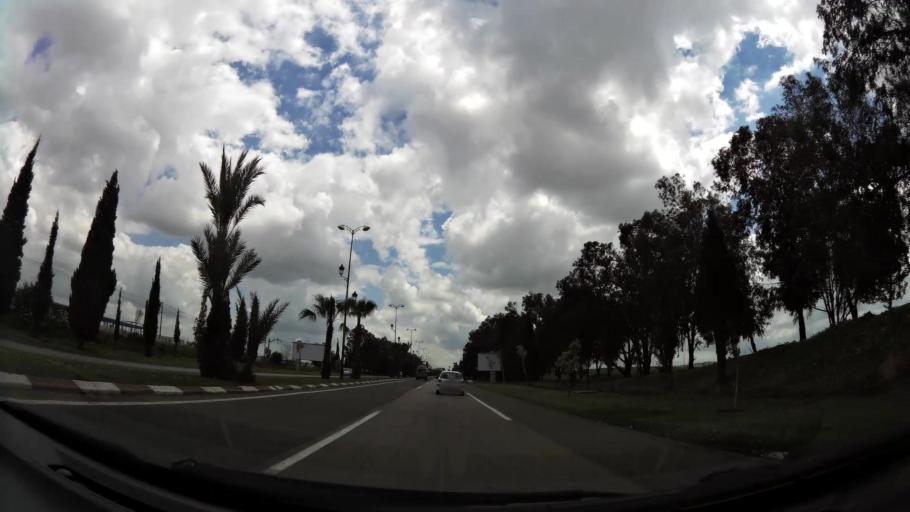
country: MA
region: Chaouia-Ouardigha
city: Nouaseur
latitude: 33.3907
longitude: -7.5667
